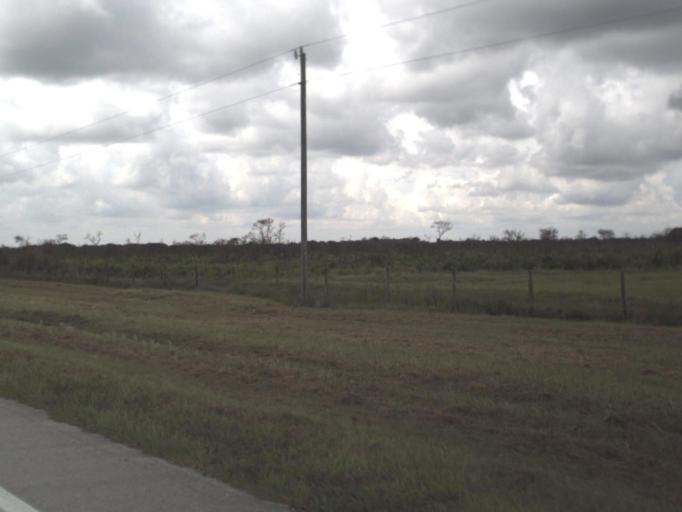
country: US
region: Florida
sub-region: Hendry County
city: Port LaBelle
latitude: 26.8796
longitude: -81.3548
